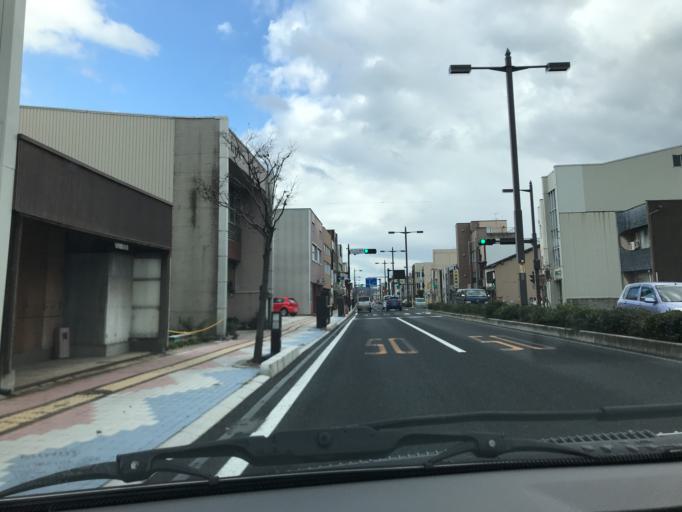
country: JP
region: Shimane
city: Matsue-shi
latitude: 35.4590
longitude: 133.0577
